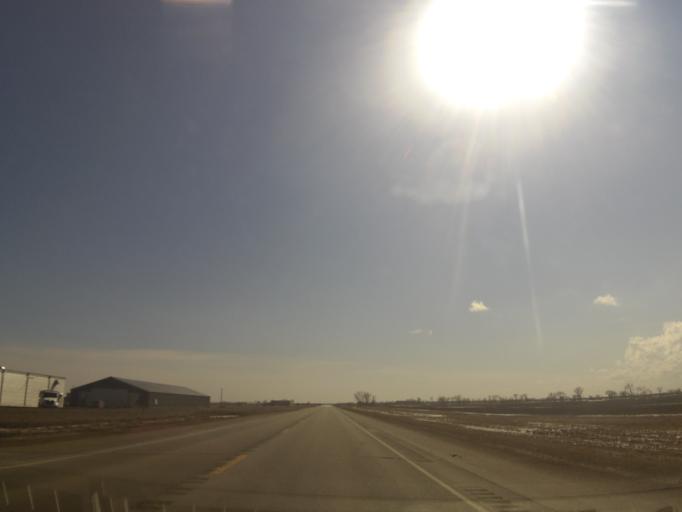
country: US
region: North Dakota
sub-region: Walsh County
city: Grafton
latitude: 48.2638
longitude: -97.3649
